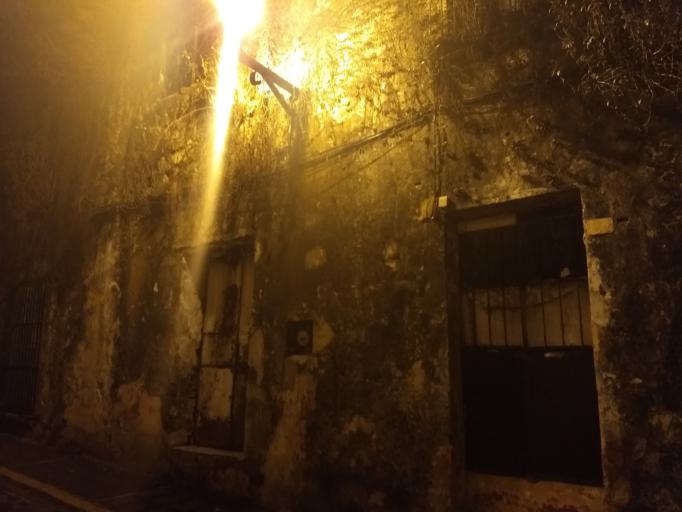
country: MX
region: Veracruz
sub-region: Xalapa
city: Xalapa de Enriquez
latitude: 19.5287
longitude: -96.9236
